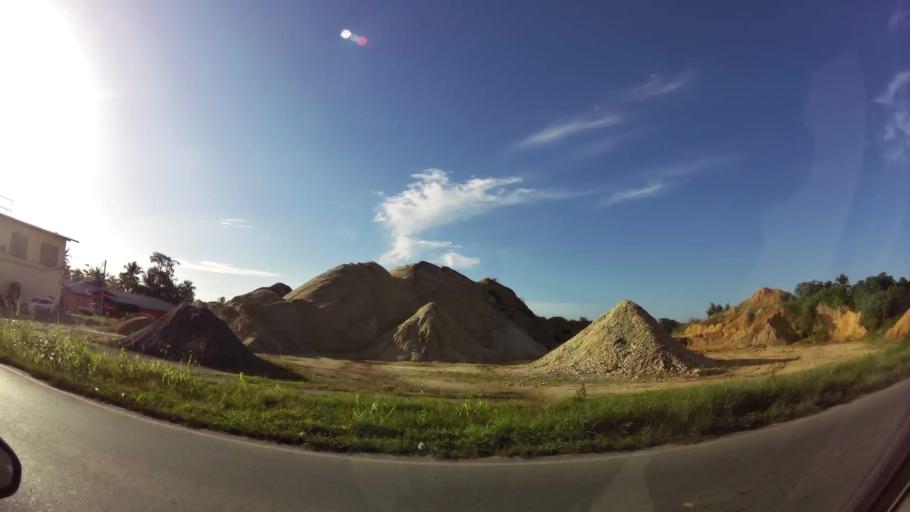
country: TT
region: Tunapuna/Piarco
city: Arouca
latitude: 10.5846
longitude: -61.3520
